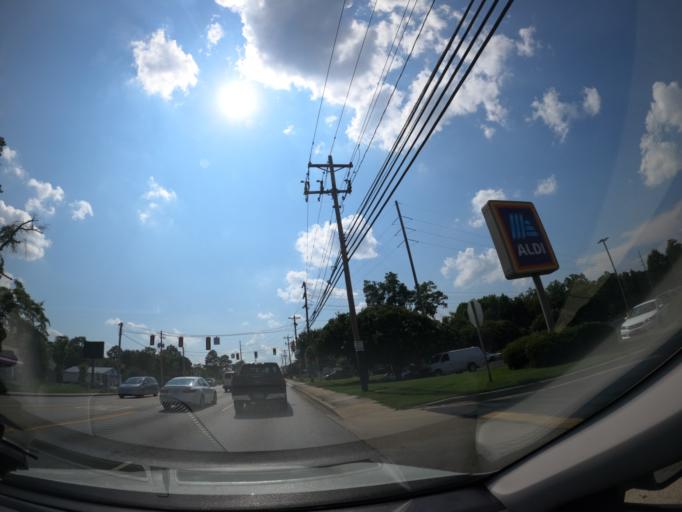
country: US
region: South Carolina
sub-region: Lexington County
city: Springdale
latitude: 33.9786
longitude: -81.1167
